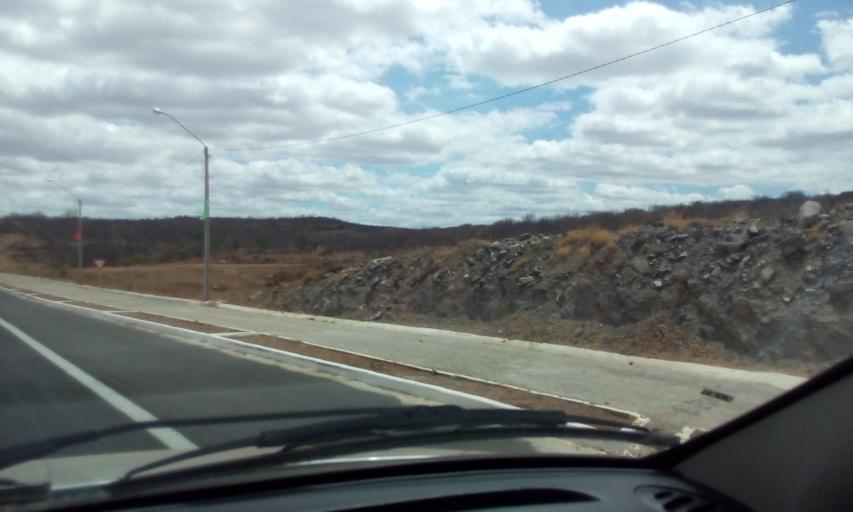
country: BR
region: Rio Grande do Norte
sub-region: Currais Novos
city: Currais Novos
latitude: -6.2570
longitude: -36.4931
